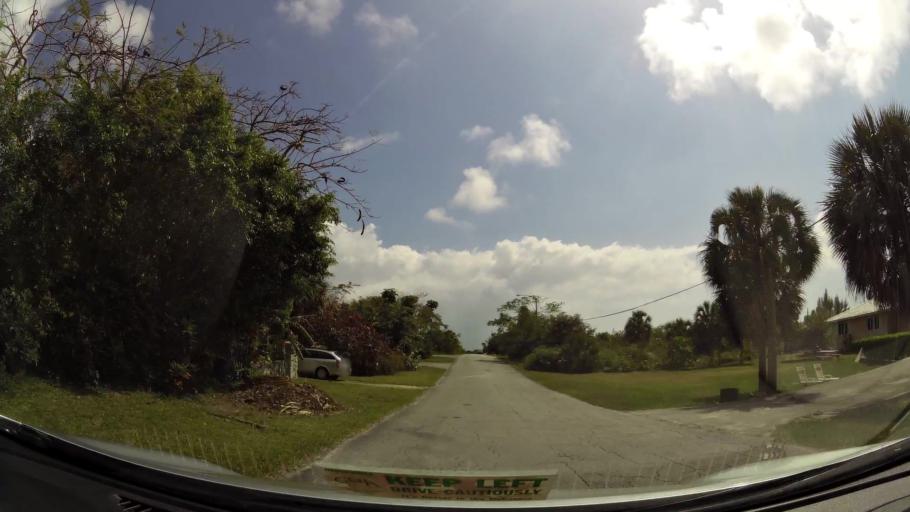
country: BS
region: Freeport
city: Freeport
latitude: 26.5138
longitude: -78.7145
